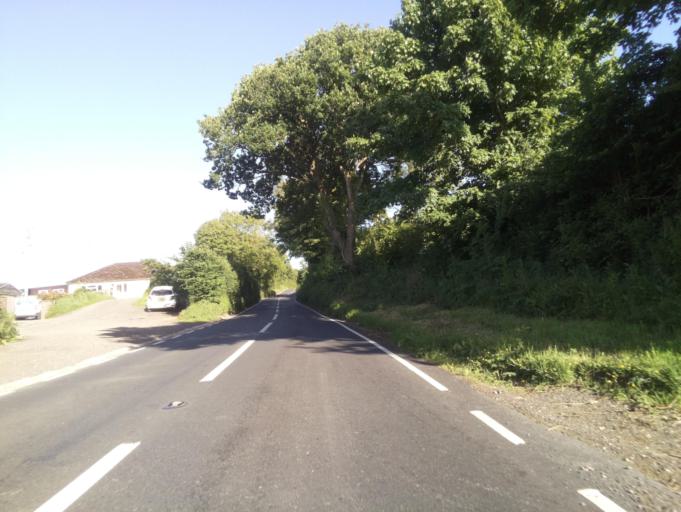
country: GB
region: England
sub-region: Devon
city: Colyton
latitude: 50.7284
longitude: -3.0387
